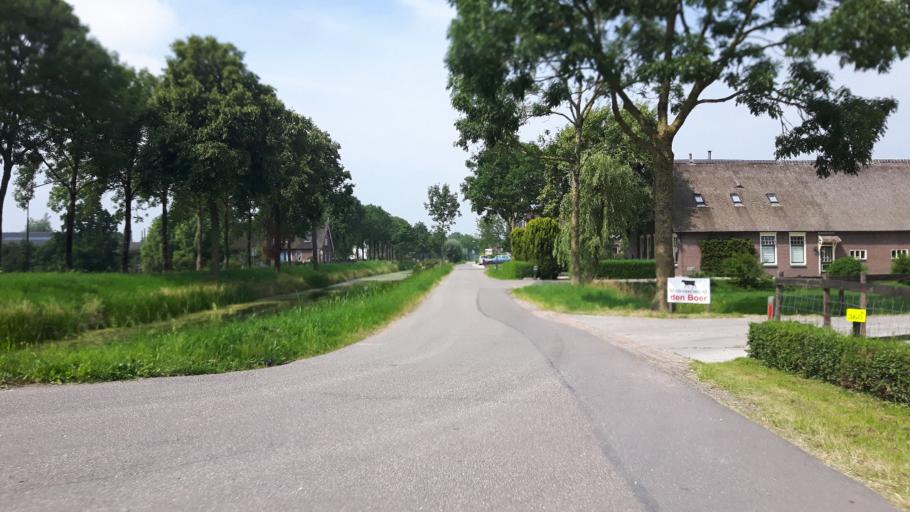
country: NL
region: Utrecht
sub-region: Gemeente Lopik
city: Lopik
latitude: 52.0032
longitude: 4.9475
